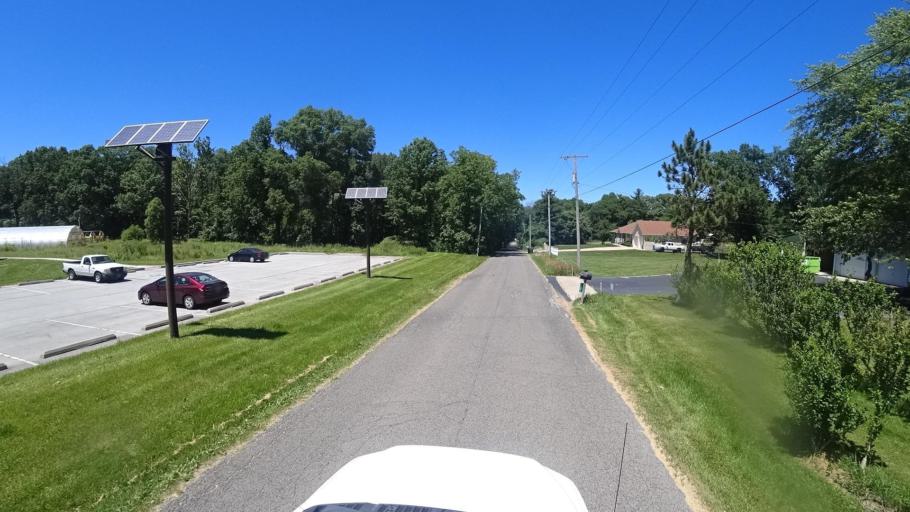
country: US
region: Indiana
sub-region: Porter County
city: Porter
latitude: 41.6326
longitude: -87.0868
